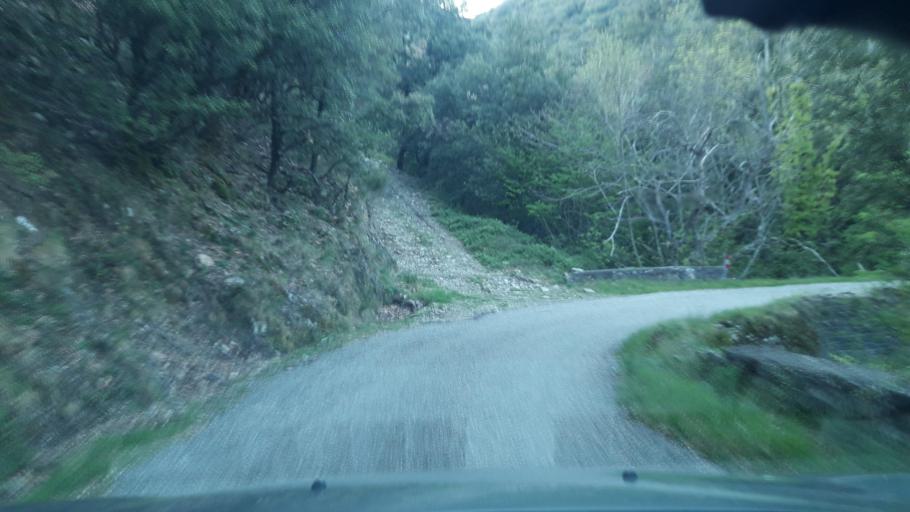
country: FR
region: Languedoc-Roussillon
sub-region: Departement du Gard
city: Valleraugue
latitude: 44.1076
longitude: 3.6797
